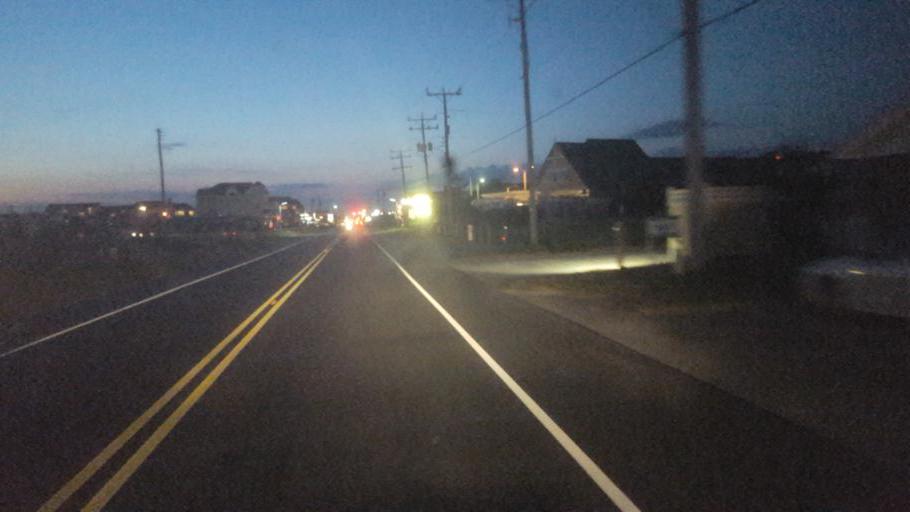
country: US
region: North Carolina
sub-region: Dare County
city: Kill Devil Hills
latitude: 36.0116
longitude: -75.6558
